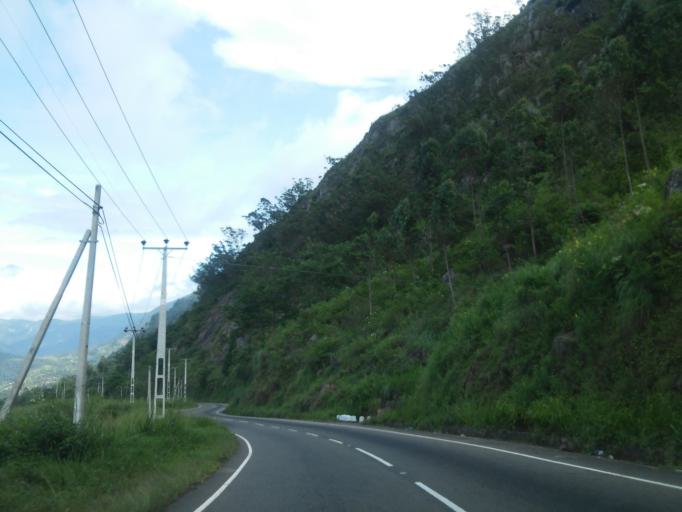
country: LK
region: Uva
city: Haputale
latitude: 6.7602
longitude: 80.9376
